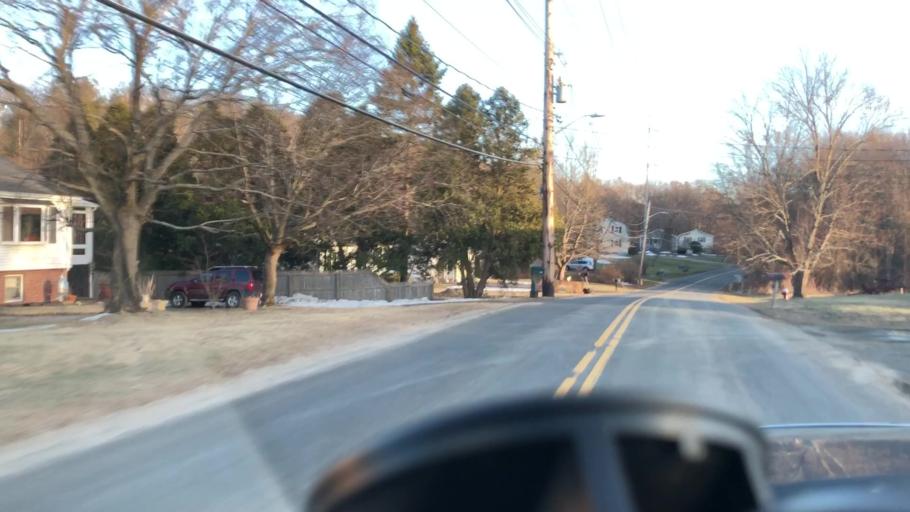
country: US
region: Massachusetts
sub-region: Hampshire County
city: Southampton
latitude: 42.2037
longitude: -72.6797
